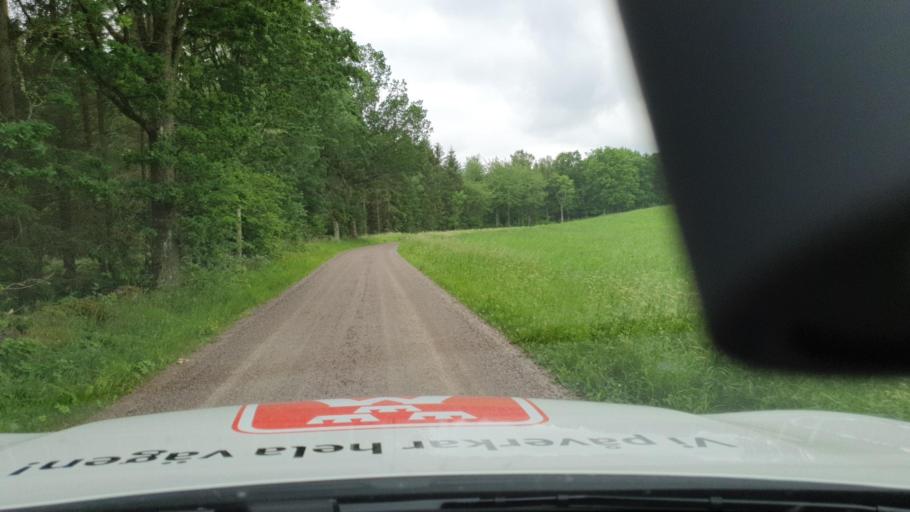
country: SE
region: Vaestra Goetaland
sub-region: Hjo Kommun
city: Hjo
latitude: 58.3620
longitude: 14.3434
